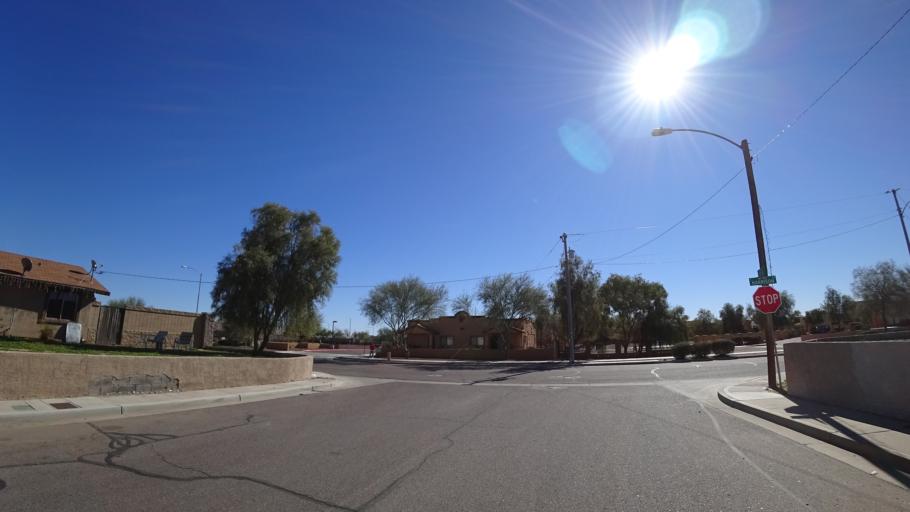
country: US
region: Arizona
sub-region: Maricopa County
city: Avondale
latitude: 33.4283
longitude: -112.3414
